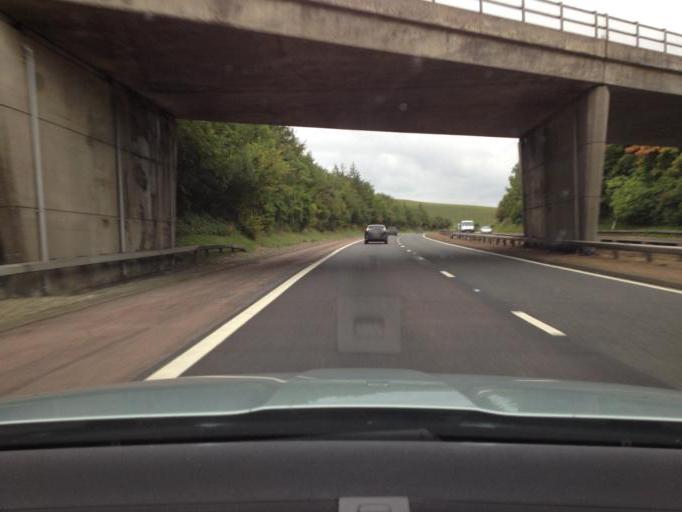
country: GB
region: Scotland
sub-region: Fife
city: Kelty
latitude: 56.1043
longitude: -3.3887
